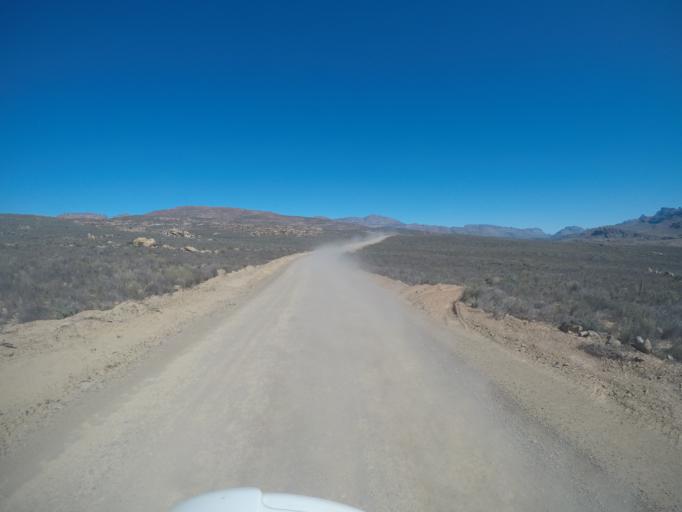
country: ZA
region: Western Cape
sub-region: West Coast District Municipality
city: Clanwilliam
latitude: -32.5053
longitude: 19.2949
